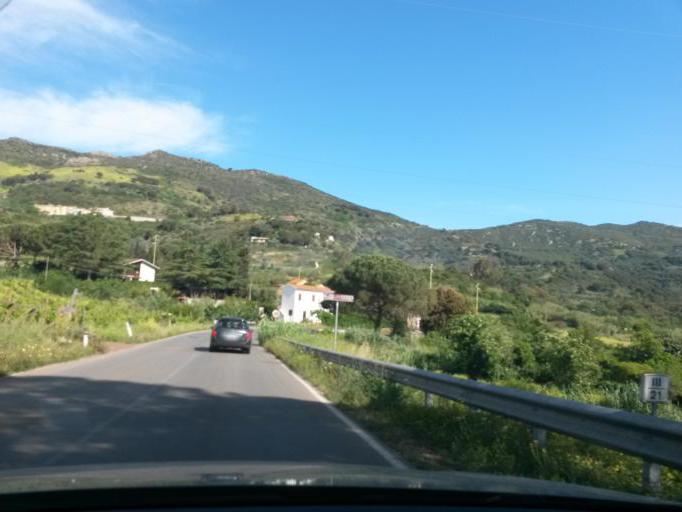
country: IT
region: Tuscany
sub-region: Provincia di Livorno
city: Rio nell'Elba
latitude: 42.8118
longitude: 10.4092
